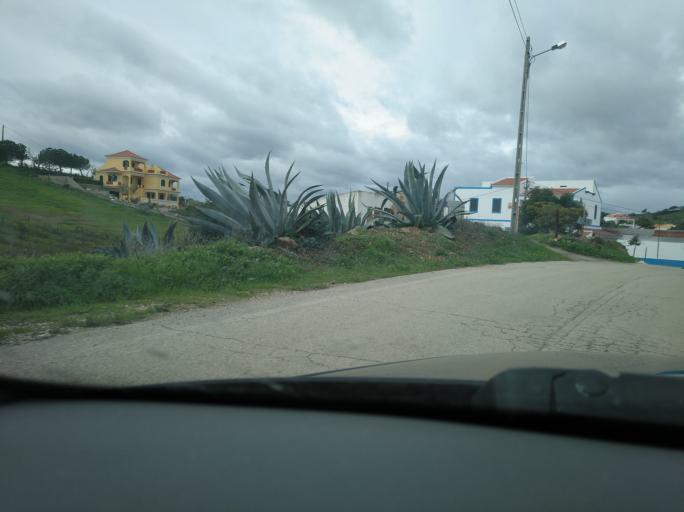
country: PT
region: Faro
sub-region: Castro Marim
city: Castro Marim
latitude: 37.2203
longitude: -7.4888
